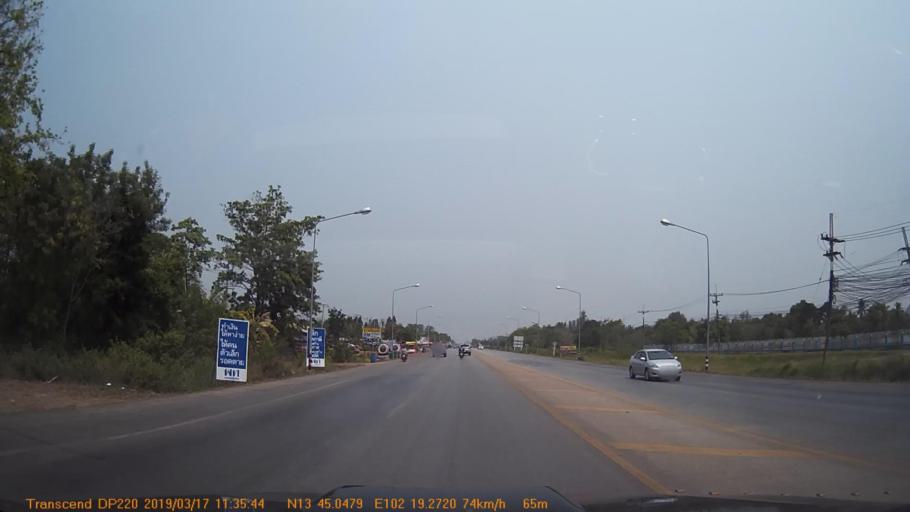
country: TH
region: Sa Kaeo
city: Watthana Nakhon
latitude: 13.7510
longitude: 102.3213
